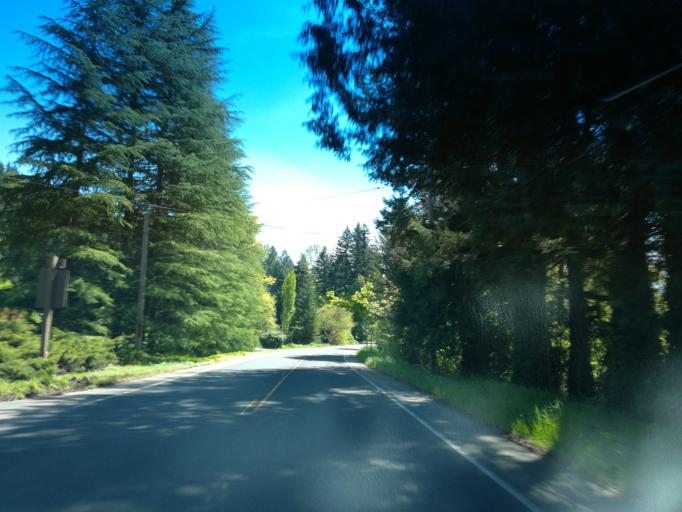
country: US
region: Oregon
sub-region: Multnomah County
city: Troutdale
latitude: 45.5299
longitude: -122.3713
